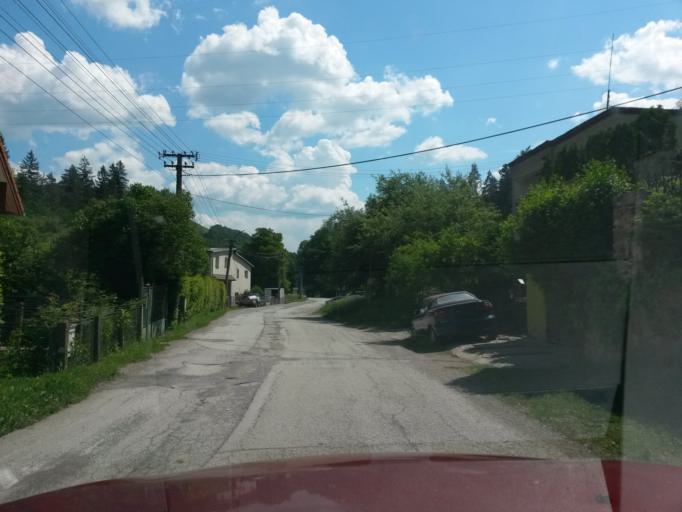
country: SK
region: Kosicky
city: Roznava
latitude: 48.6825
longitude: 20.5417
